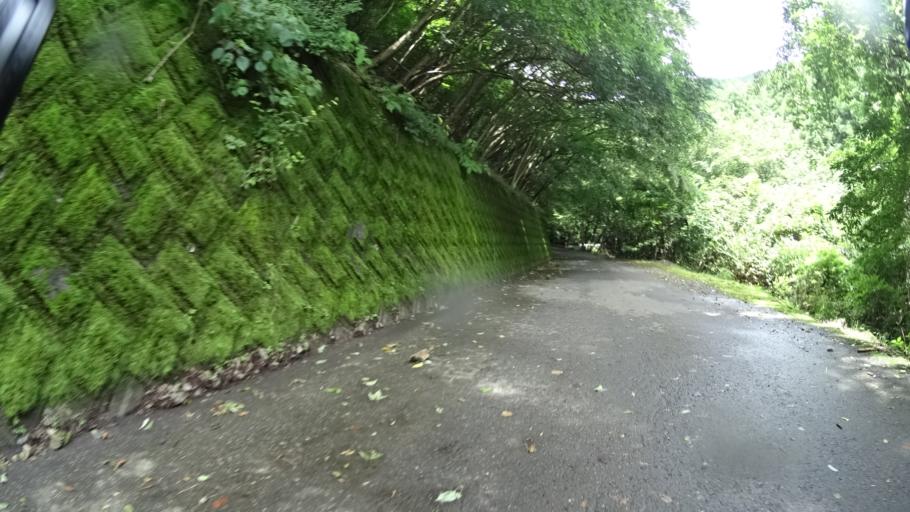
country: JP
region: Saitama
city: Chichibu
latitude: 35.8902
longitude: 139.1366
